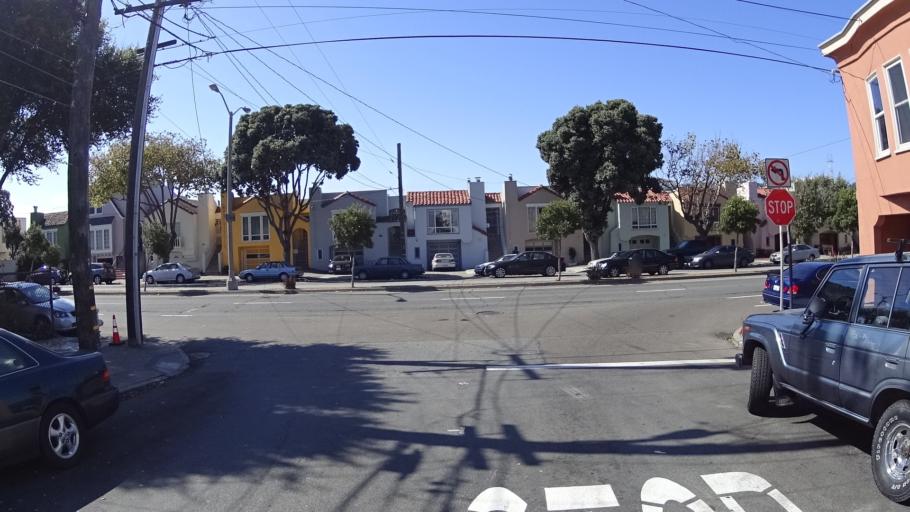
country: US
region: California
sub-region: San Mateo County
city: Daly City
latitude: 37.7254
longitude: -122.4365
